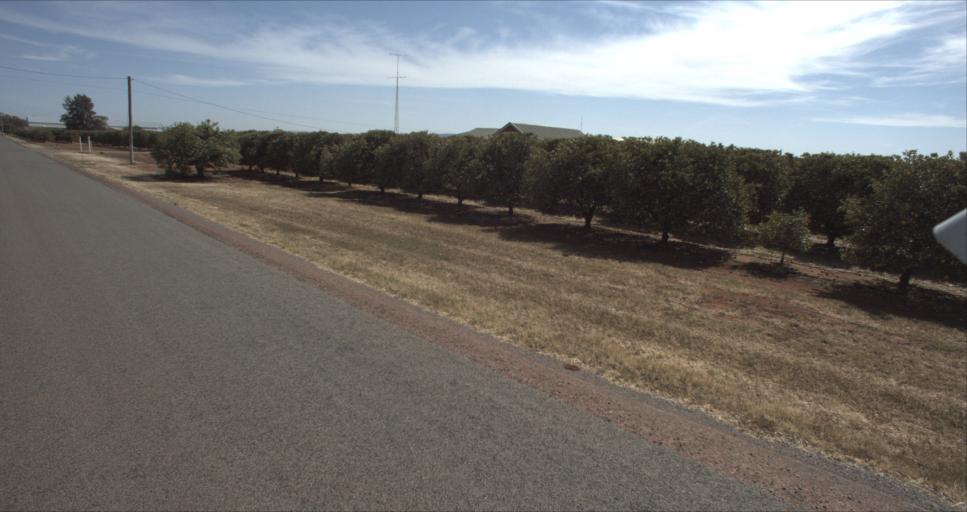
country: AU
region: New South Wales
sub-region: Leeton
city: Leeton
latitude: -34.5827
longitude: 146.4703
